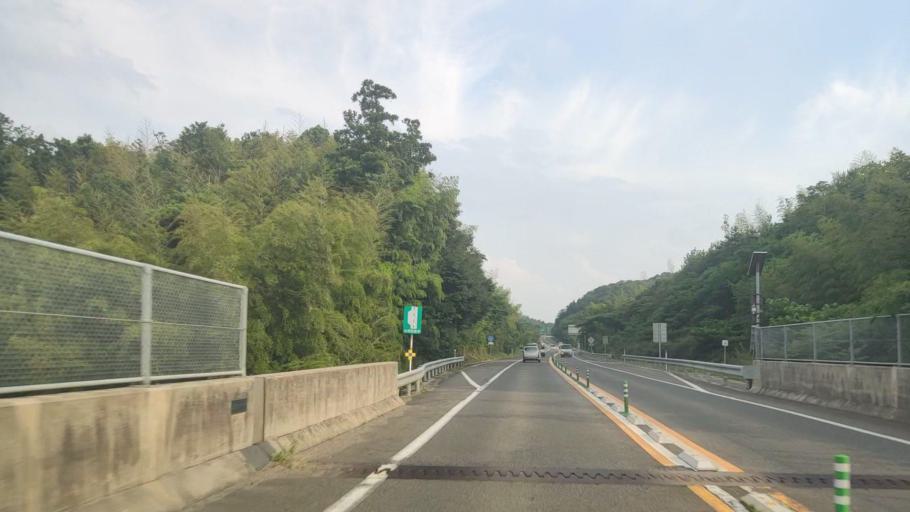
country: JP
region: Tottori
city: Kurayoshi
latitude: 35.4617
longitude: 133.8095
